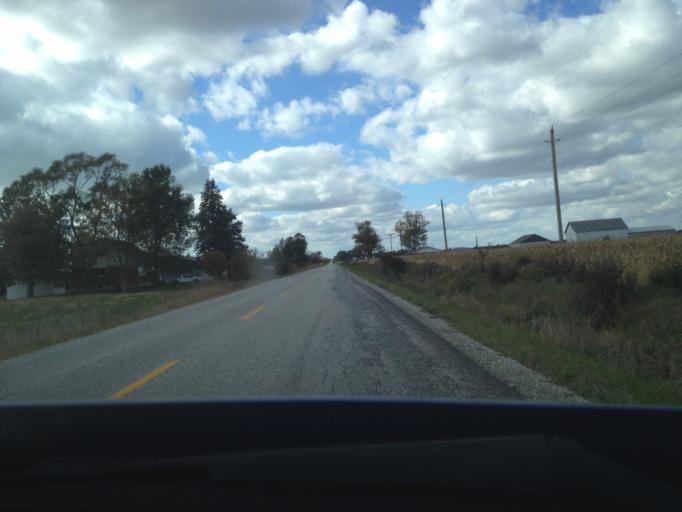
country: US
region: Michigan
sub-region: Wayne County
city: Grosse Pointe
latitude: 42.0315
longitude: -82.5346
